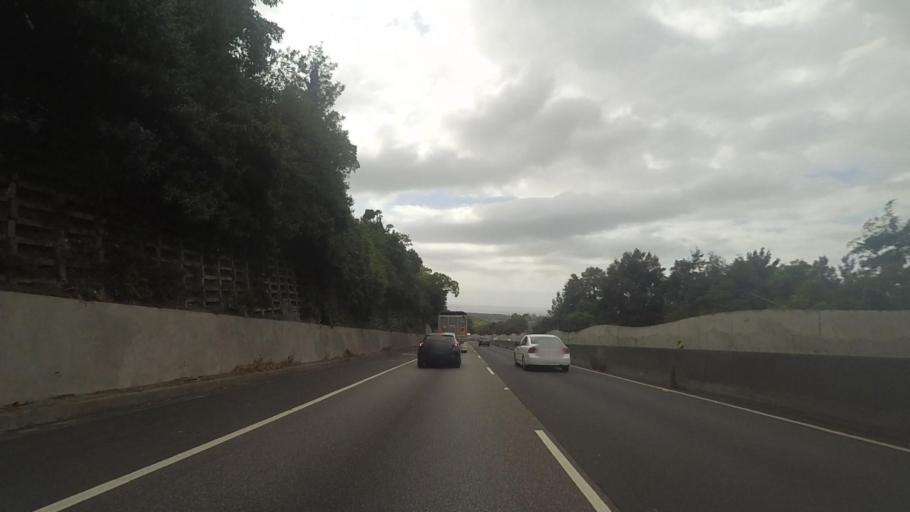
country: AU
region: New South Wales
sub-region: Wollongong
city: Mount Ousley
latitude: -34.4012
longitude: 150.8714
